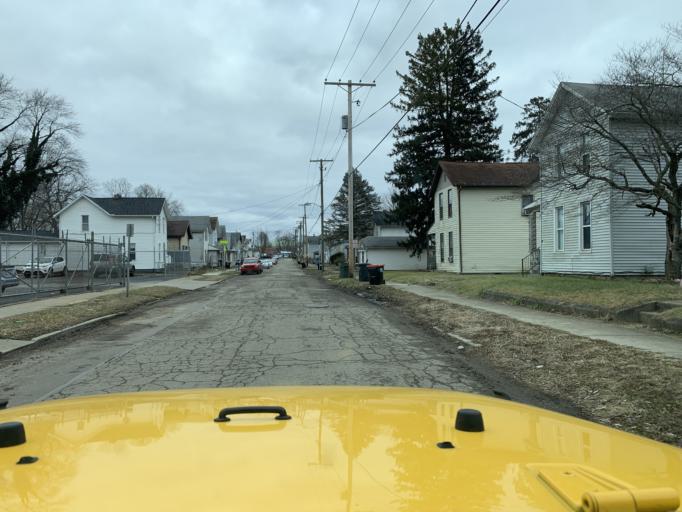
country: US
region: Ohio
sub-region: Licking County
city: Newark
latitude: 40.0544
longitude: -82.4113
